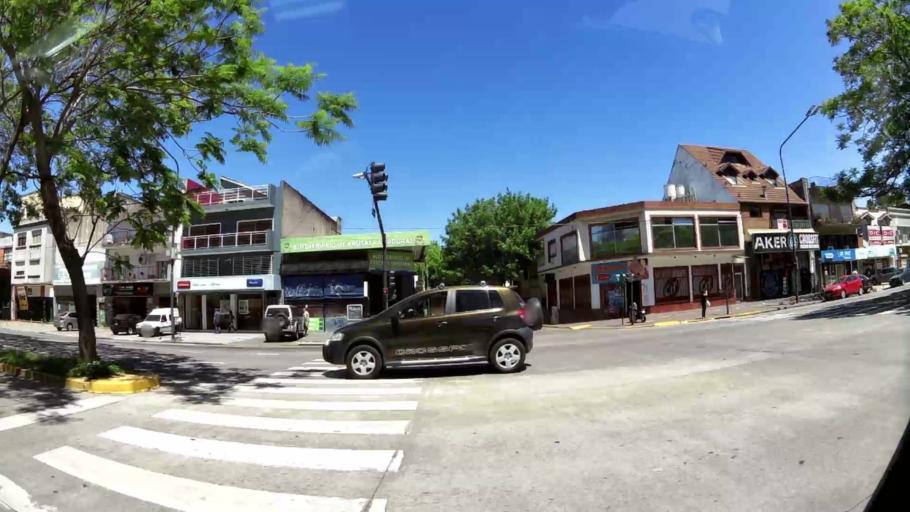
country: AR
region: Buenos Aires
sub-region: Partido de Vicente Lopez
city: Olivos
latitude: -34.4995
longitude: -58.4967
